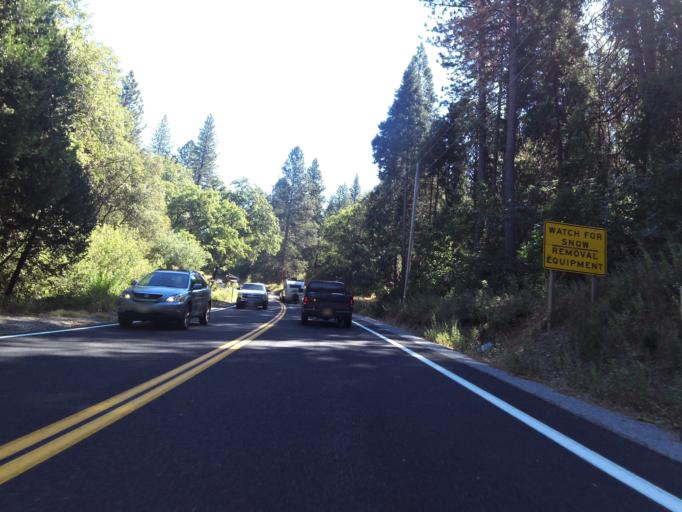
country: US
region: California
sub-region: Calaveras County
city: Forest Meadows
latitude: 38.1650
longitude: -120.4240
